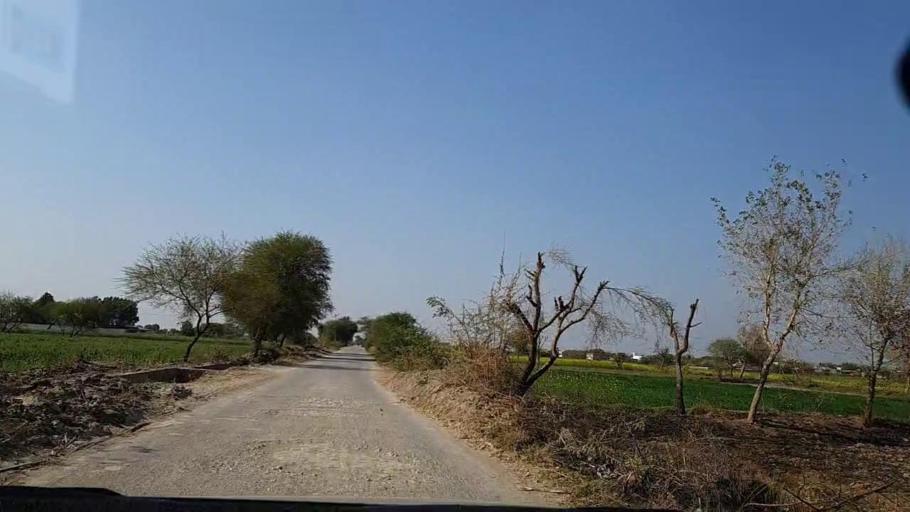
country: PK
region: Sindh
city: Digri
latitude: 25.1621
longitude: 69.0723
